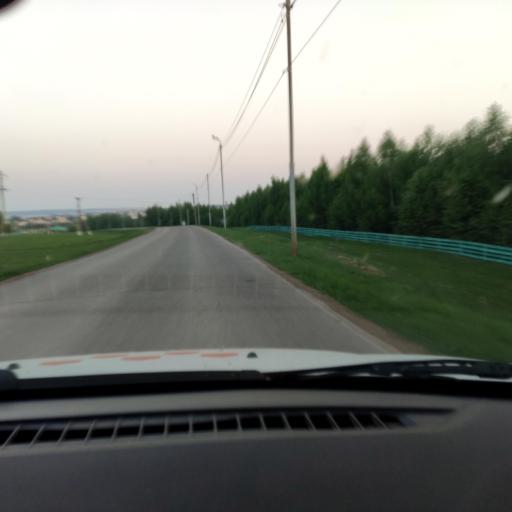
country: RU
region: Bashkortostan
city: Karmaskaly
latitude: 54.3761
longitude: 56.1511
